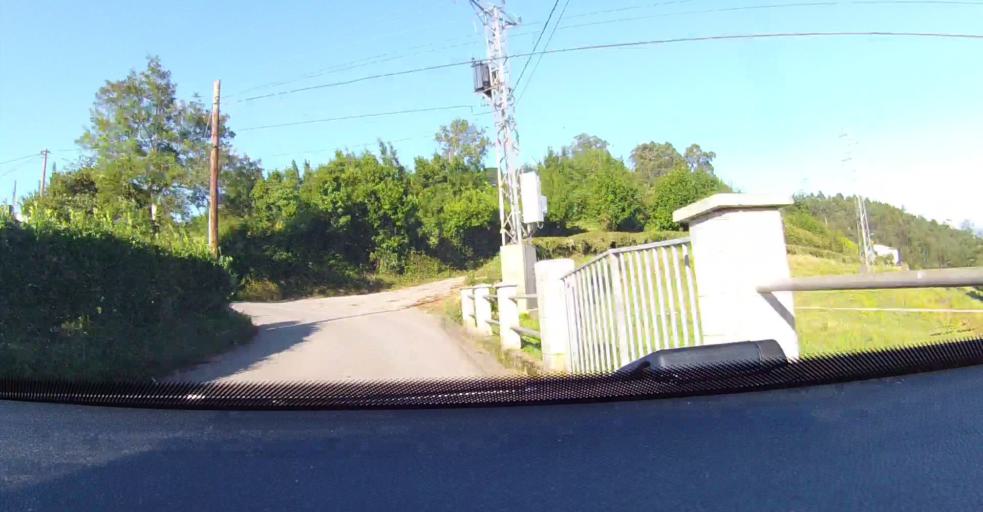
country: ES
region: Asturias
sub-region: Province of Asturias
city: Villaviciosa
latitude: 43.4846
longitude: -5.4068
